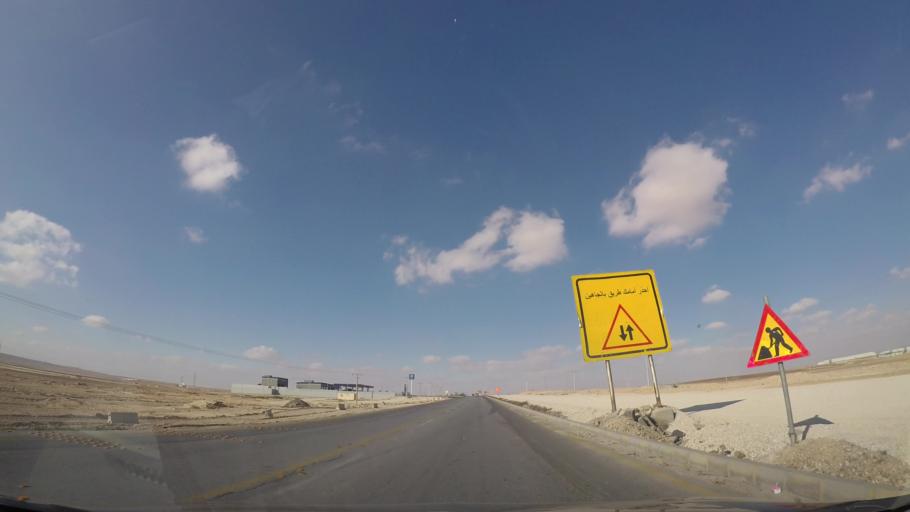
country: JO
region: Karak
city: Adir
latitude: 31.2776
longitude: 36.0542
